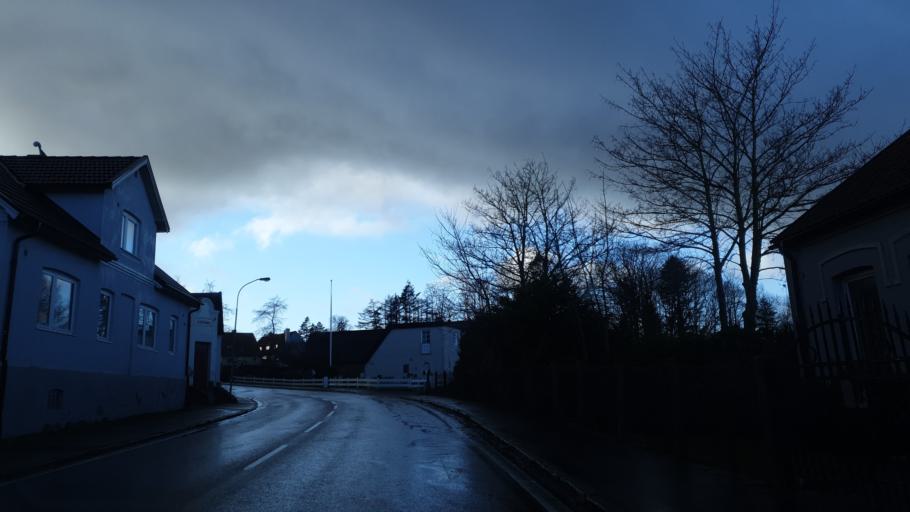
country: SE
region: Skane
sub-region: Skurups Kommun
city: Rydsgard
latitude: 55.4728
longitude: 13.5854
